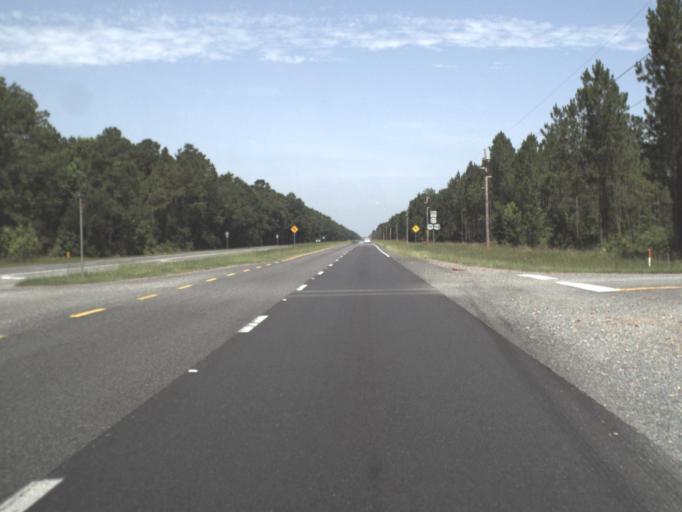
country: US
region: Florida
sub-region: Dixie County
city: Cross City
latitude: 29.6537
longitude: -83.1752
